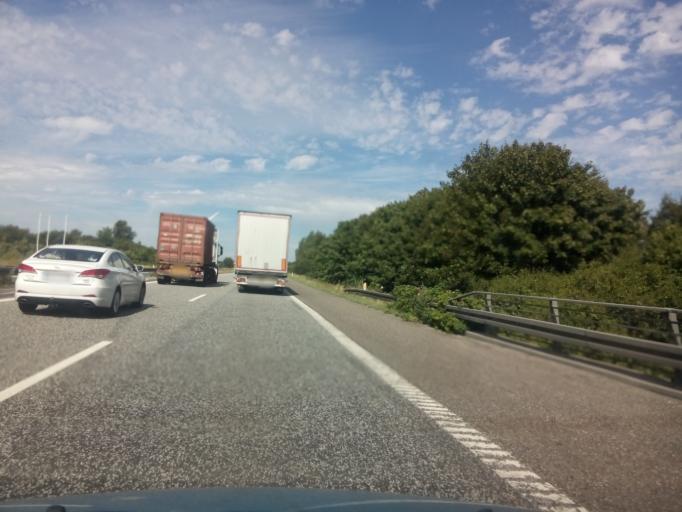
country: DK
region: Central Jutland
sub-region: Randers Kommune
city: Randers
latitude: 56.4247
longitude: 10.0527
